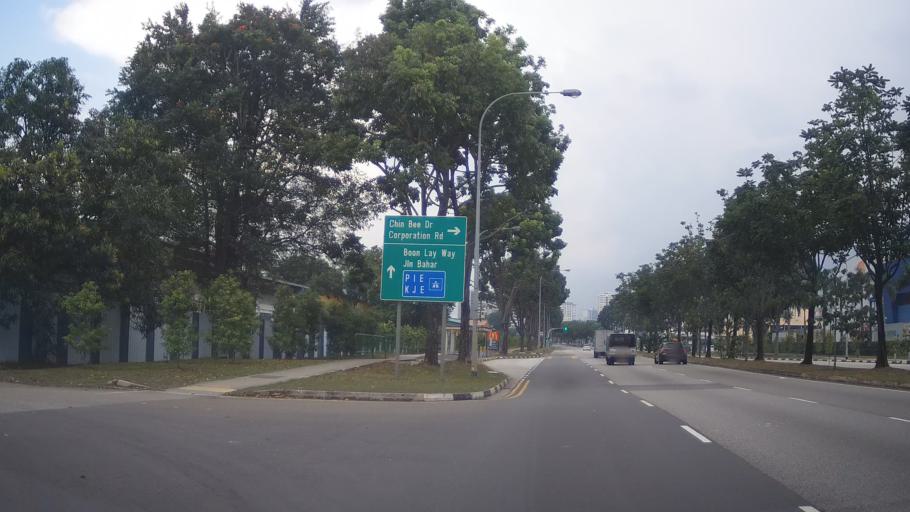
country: MY
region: Johor
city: Johor Bahru
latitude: 1.3334
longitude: 103.7079
